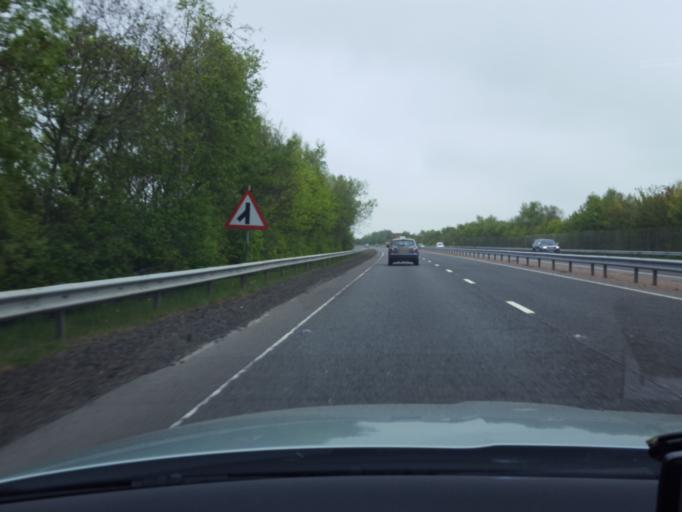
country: GB
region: Scotland
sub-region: Angus
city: Forfar
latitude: 56.6027
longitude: -2.9053
